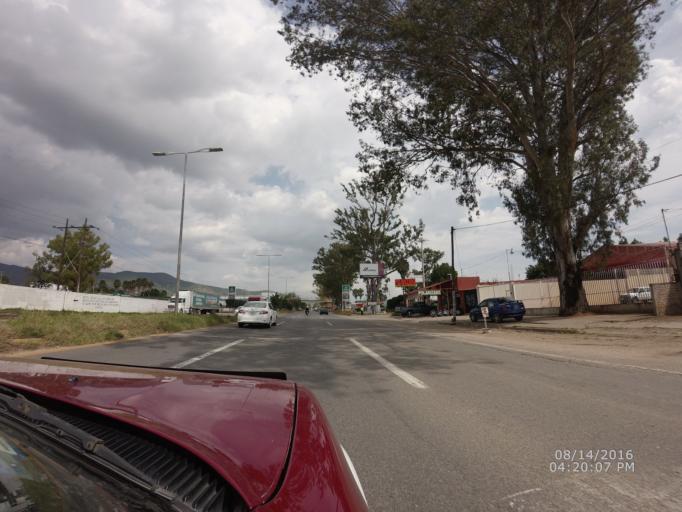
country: MX
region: Oaxaca
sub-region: Santa Maria Atzompa
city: Fraccionamiento Riberas de San Jeronimo
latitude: 17.1298
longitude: -96.7704
